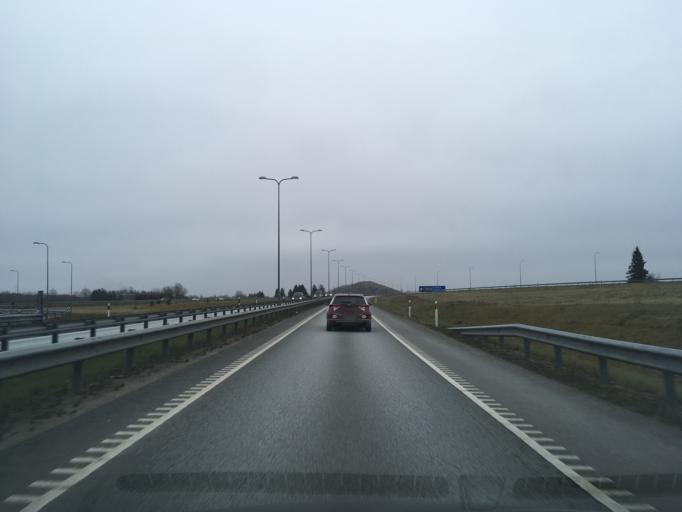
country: EE
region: Ida-Virumaa
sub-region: Kohtla-Jaerve linn
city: Kohtla-Jarve
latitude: 59.4036
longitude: 27.3271
